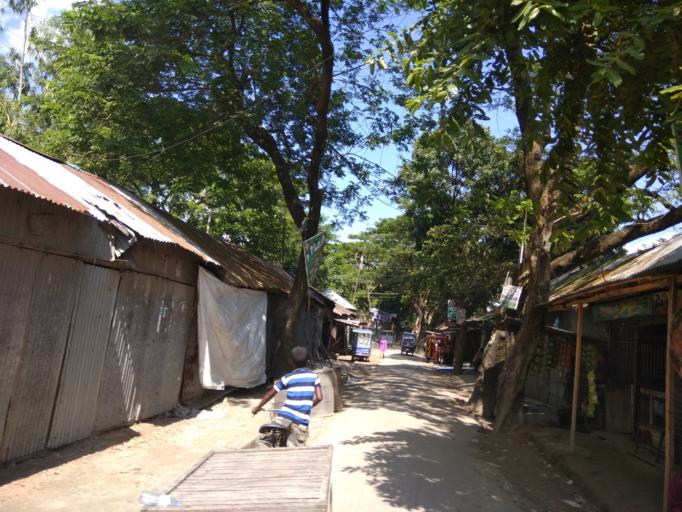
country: BD
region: Dhaka
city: Narayanganj
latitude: 23.4448
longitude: 90.4508
